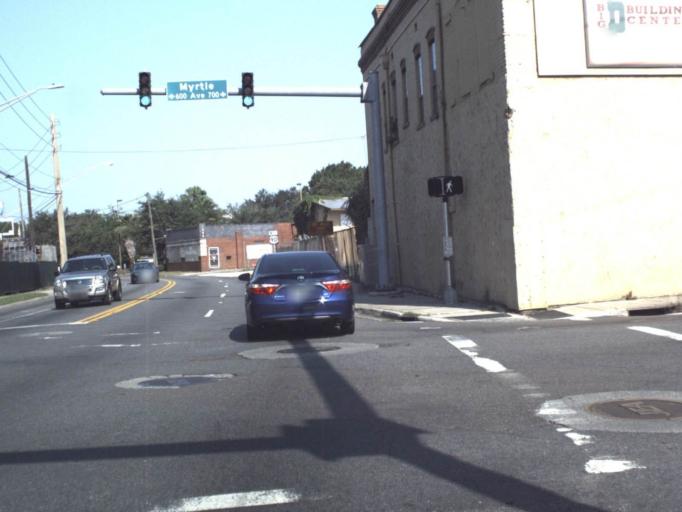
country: US
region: Florida
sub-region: Duval County
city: Jacksonville
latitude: 30.3364
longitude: -81.6759
